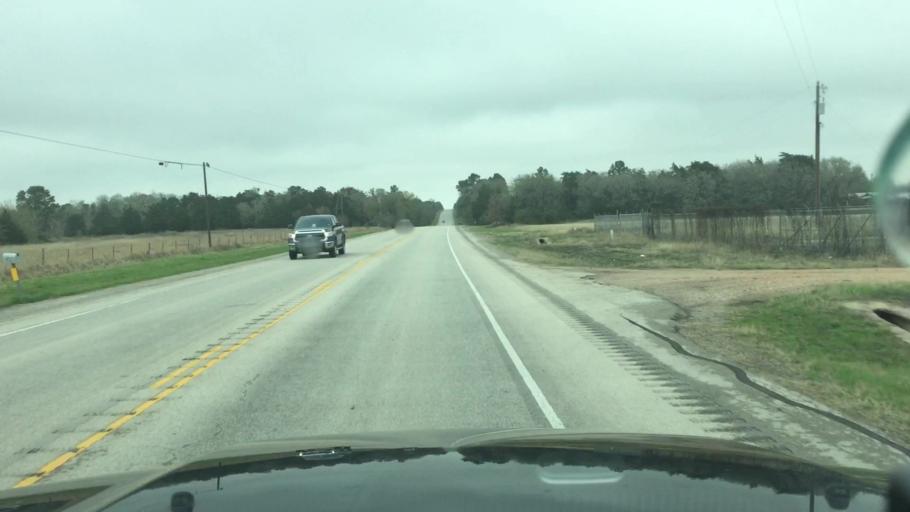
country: US
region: Texas
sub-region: Lee County
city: Giddings
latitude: 30.0648
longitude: -96.9164
